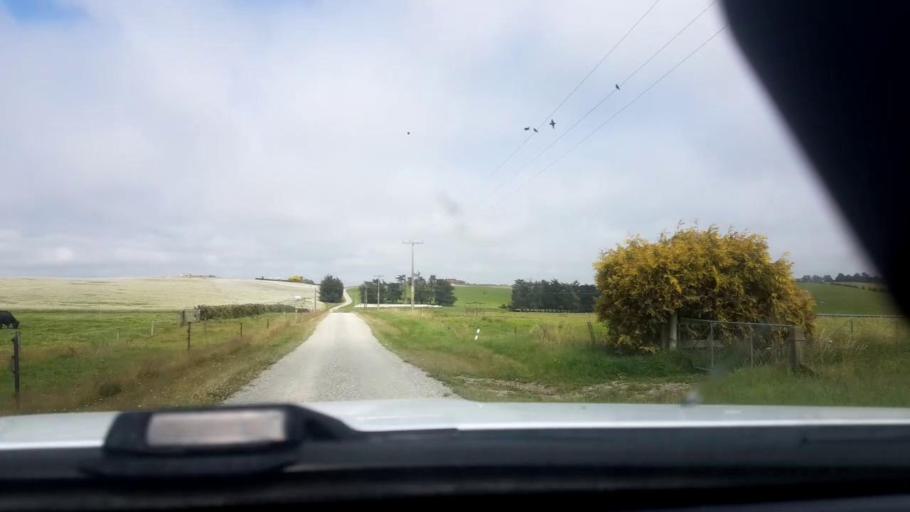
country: NZ
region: Canterbury
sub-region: Timaru District
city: Timaru
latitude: -44.3297
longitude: 171.2023
